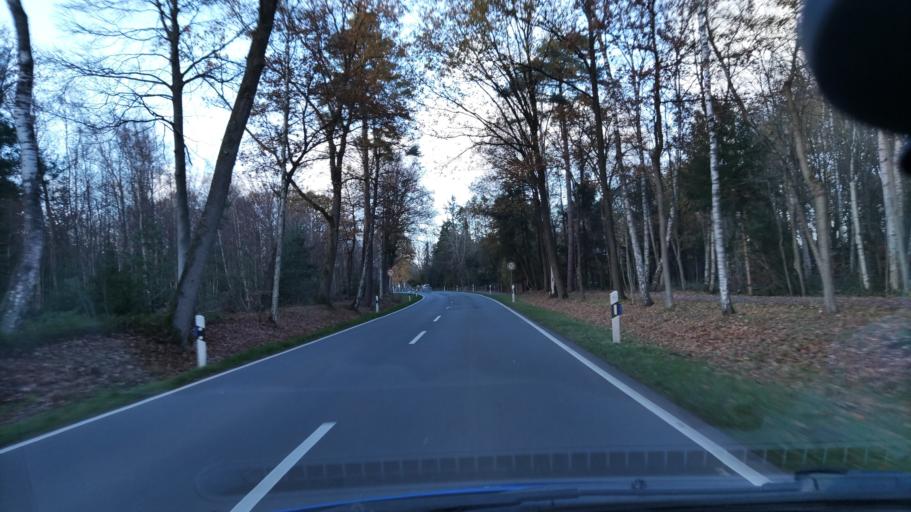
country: DE
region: Lower Saxony
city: Schneverdingen
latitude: 53.0735
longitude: 9.8141
